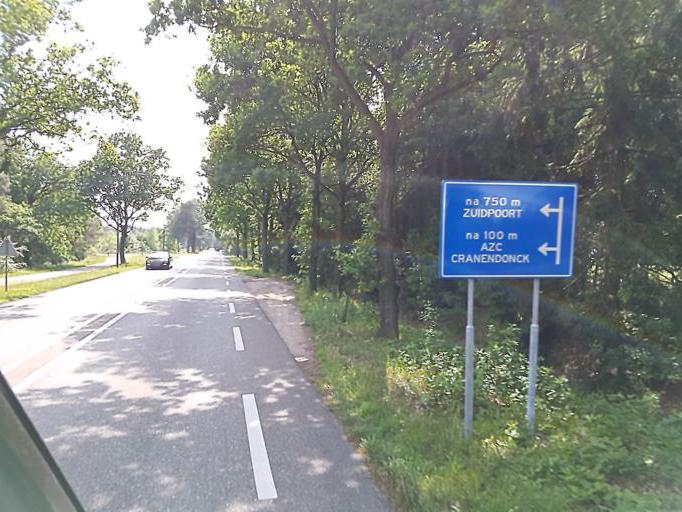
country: NL
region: North Brabant
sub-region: Gemeente Cranendonck
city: Cranendonck
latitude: 51.2917
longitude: 5.6309
